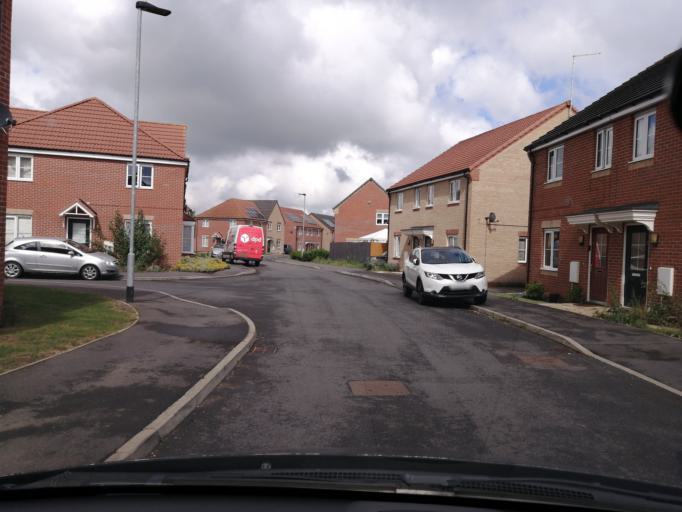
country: GB
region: England
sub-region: Peterborough
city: Peterborough
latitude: 52.5563
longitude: -0.2418
